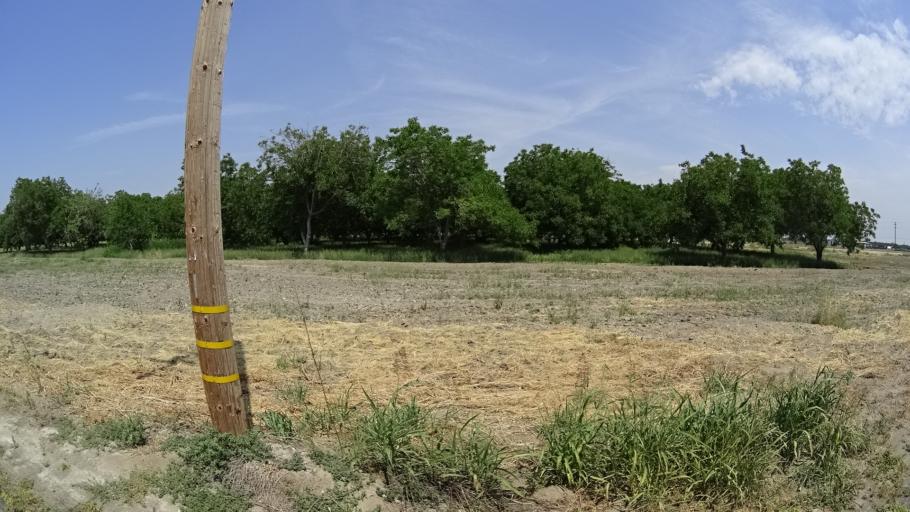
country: US
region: California
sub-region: Kings County
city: Armona
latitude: 36.3180
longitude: -119.6935
